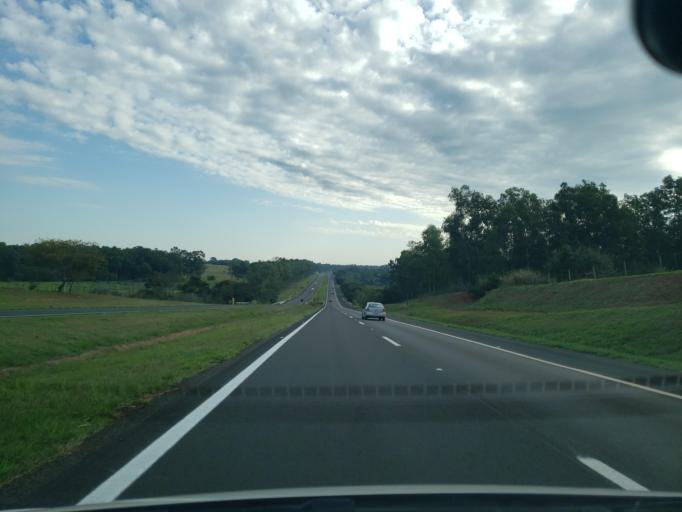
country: BR
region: Sao Paulo
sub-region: Guararapes
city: Guararapes
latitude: -21.2102
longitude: -50.6695
